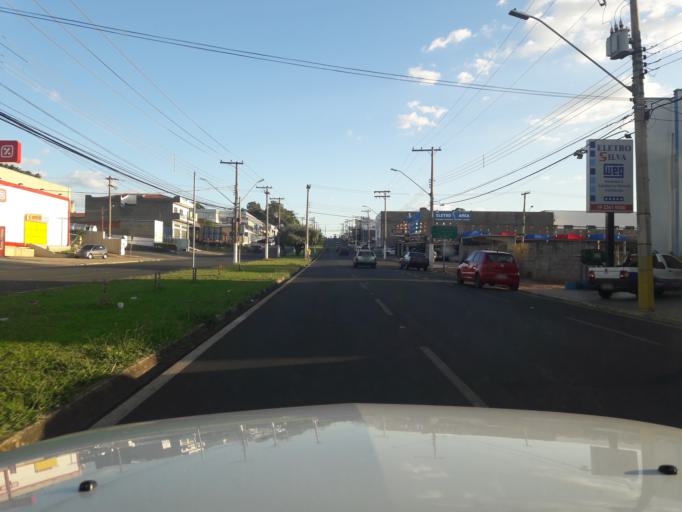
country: BR
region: Sao Paulo
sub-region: Moji-Guacu
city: Mogi-Gaucu
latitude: -22.3861
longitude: -46.9436
